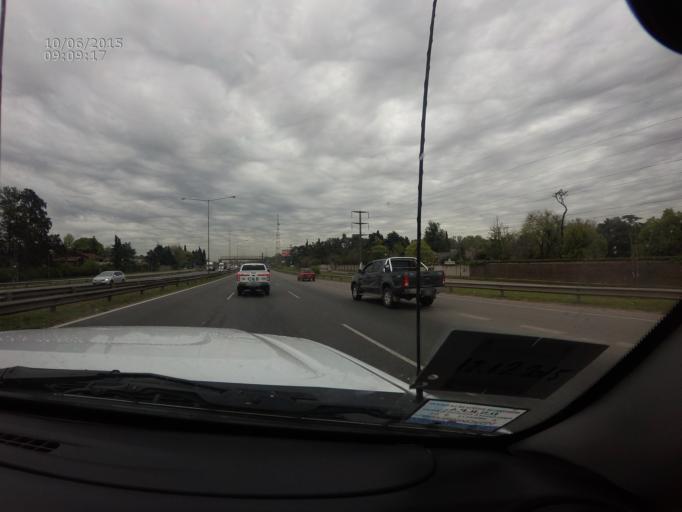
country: AR
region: Buenos Aires
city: Santa Catalina - Dique Lujan
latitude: -34.3789
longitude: -58.7526
